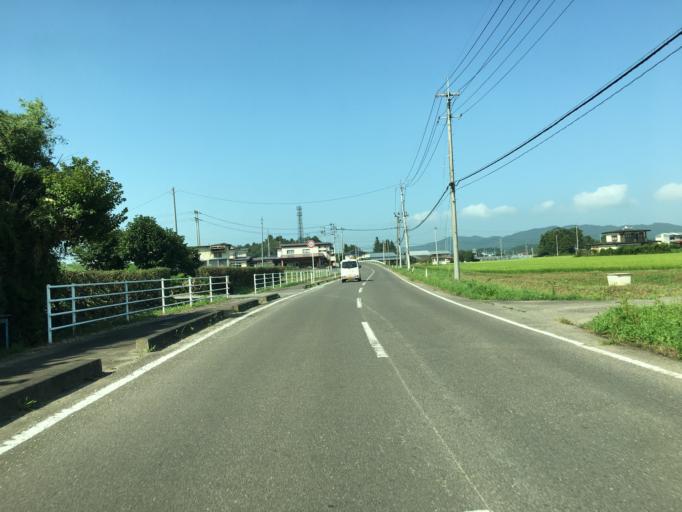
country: JP
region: Miyagi
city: Kakuda
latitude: 37.9560
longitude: 140.7960
